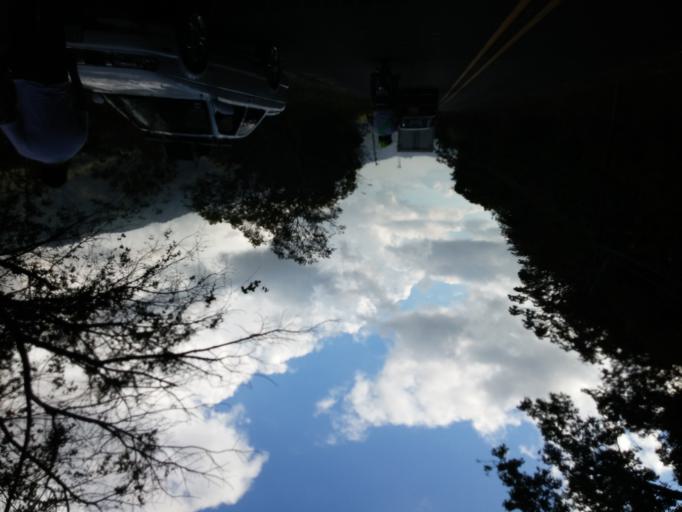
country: CR
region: San Jose
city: San Ignacio
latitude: 9.7984
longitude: -84.1589
